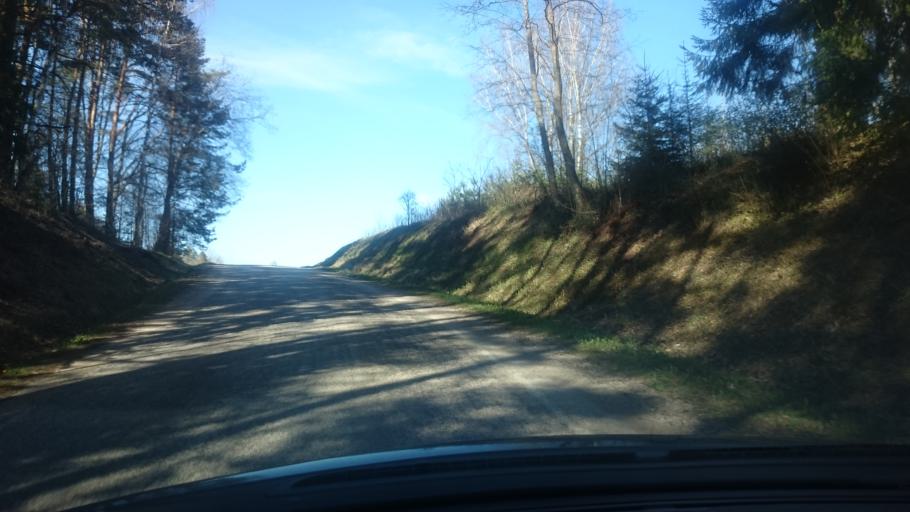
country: EE
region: Polvamaa
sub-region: Polva linn
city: Polva
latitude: 58.1399
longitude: 27.0205
